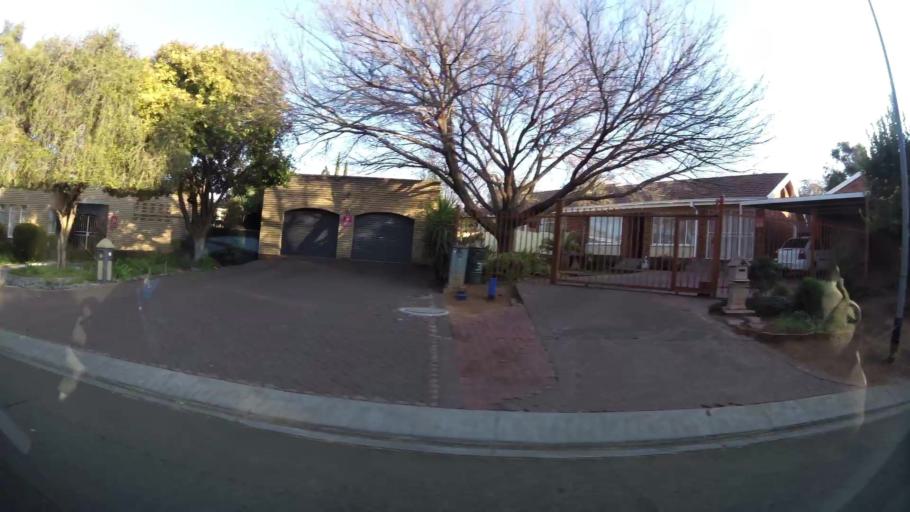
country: ZA
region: Orange Free State
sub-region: Mangaung Metropolitan Municipality
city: Bloemfontein
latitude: -29.1454
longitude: 26.1648
